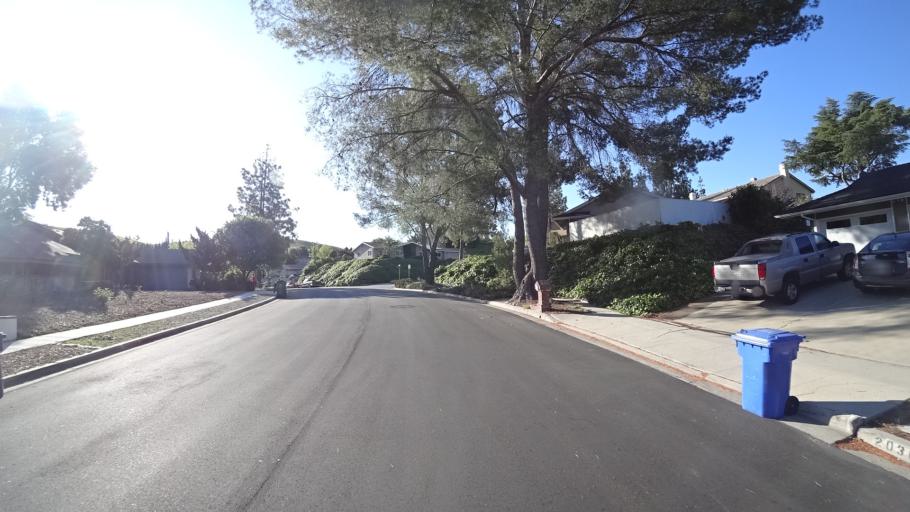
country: US
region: California
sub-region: Ventura County
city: Thousand Oaks
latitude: 34.1883
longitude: -118.8428
